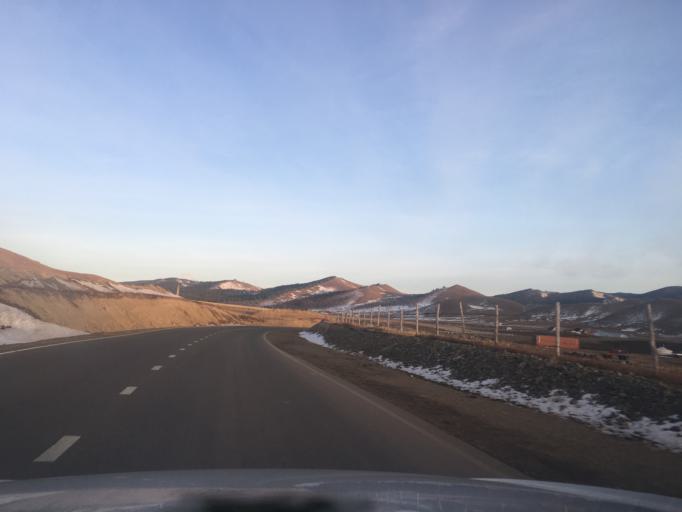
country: MN
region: Ulaanbaatar
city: Ulaanbaatar
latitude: 48.1055
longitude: 106.7315
